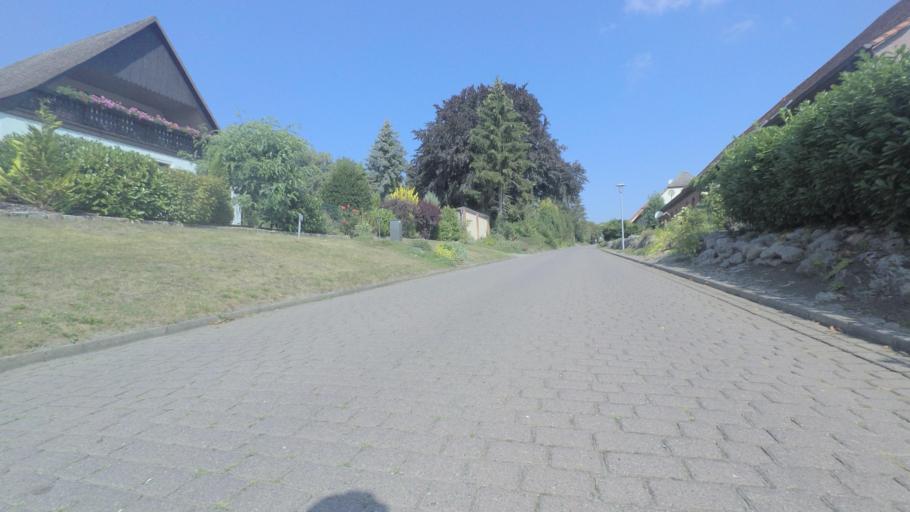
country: DE
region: Mecklenburg-Vorpommern
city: Pampow
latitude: 53.6813
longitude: 12.5669
